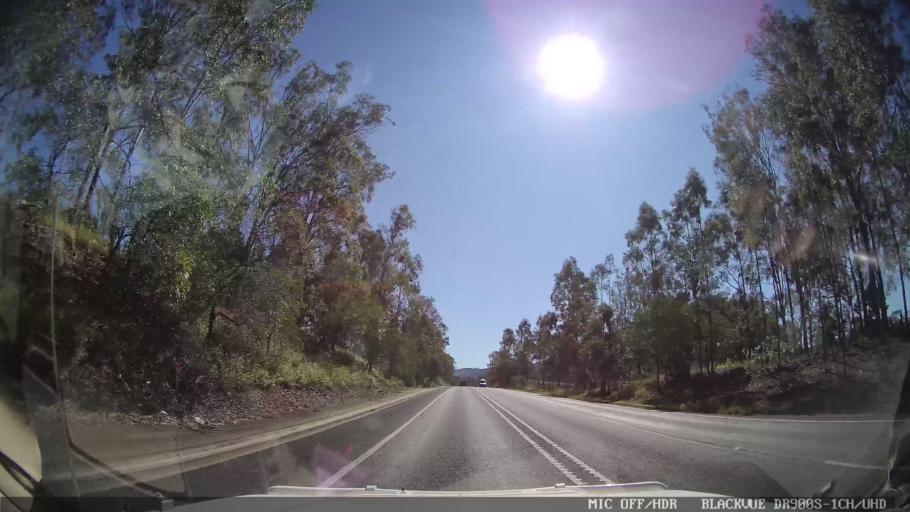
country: AU
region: Queensland
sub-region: Gympie Regional Council
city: Gympie
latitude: -26.0008
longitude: 152.5665
